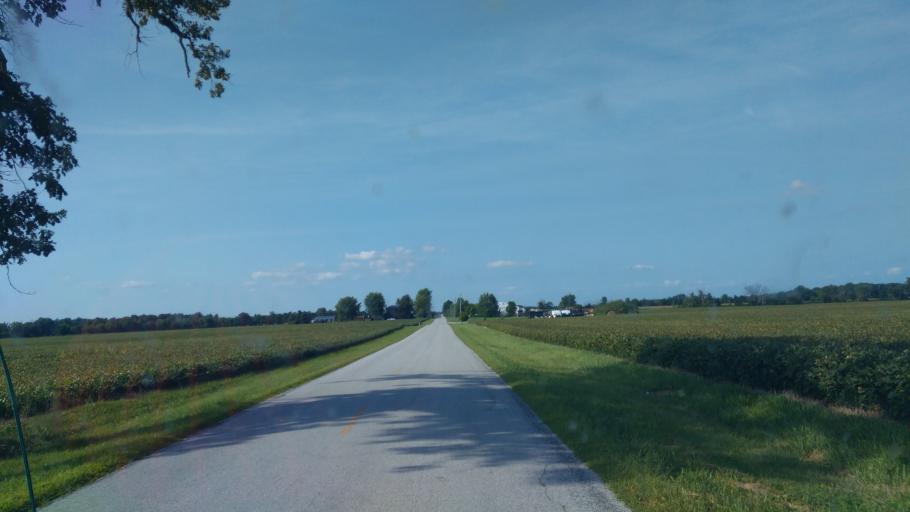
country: US
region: Ohio
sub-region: Hardin County
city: Forest
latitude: 40.7403
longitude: -83.5763
